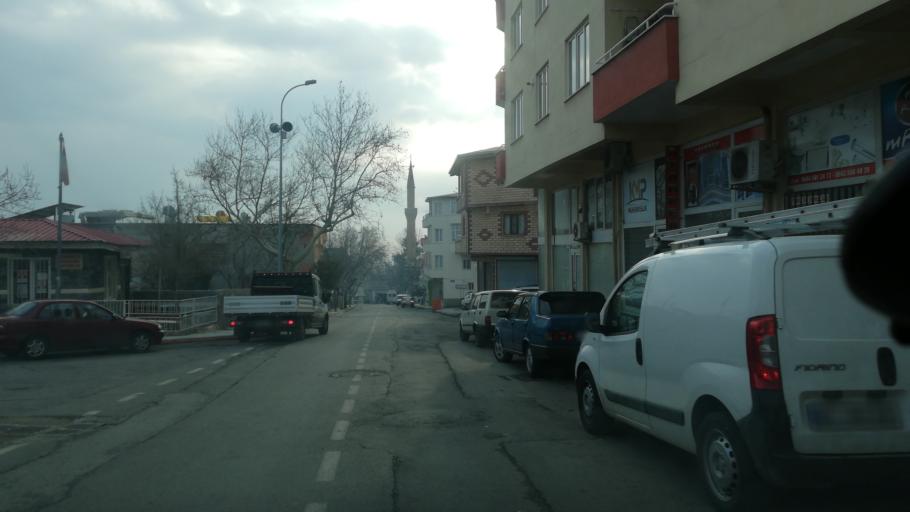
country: TR
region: Kahramanmaras
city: Kahramanmaras
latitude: 37.5900
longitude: 36.9089
